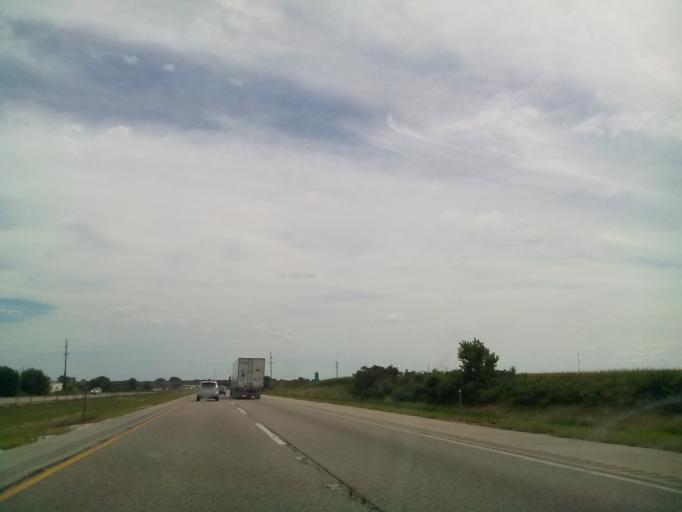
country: US
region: Illinois
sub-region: Kane County
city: Maple Park
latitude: 41.8829
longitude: -88.6236
